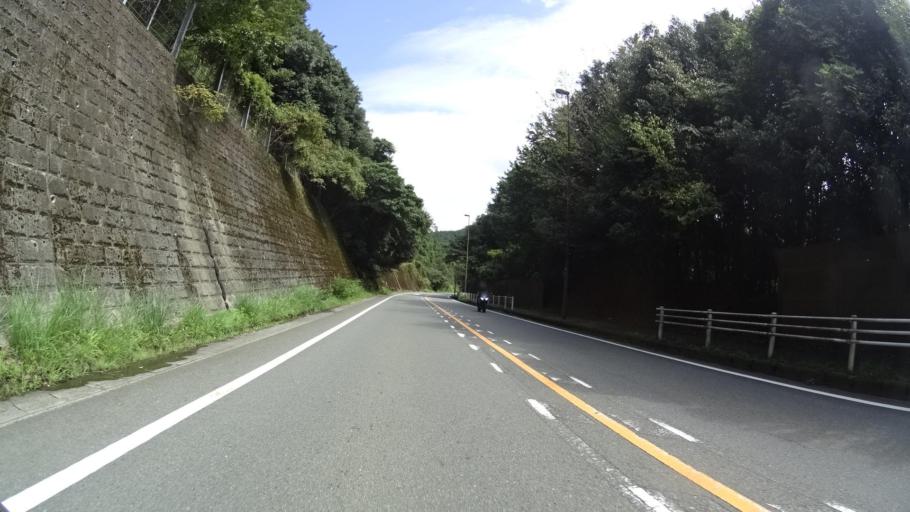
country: JP
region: Kyoto
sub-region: Kyoto-shi
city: Kamigyo-ku
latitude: 35.0897
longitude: 135.7585
